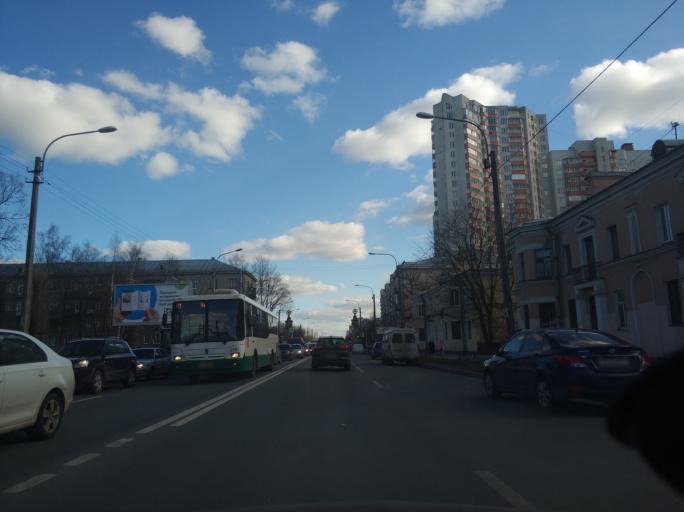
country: RU
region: St.-Petersburg
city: Krasnogvargeisky
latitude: 59.9609
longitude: 30.4897
